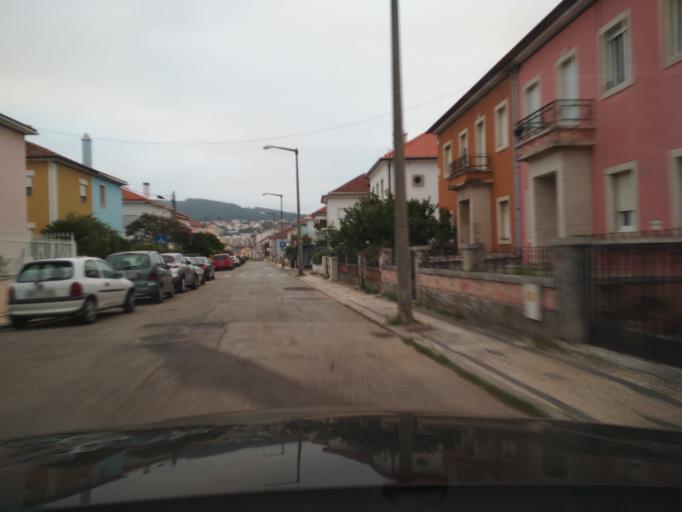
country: PT
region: Coimbra
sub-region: Coimbra
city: Coimbra
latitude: 40.1977
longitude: -8.4080
